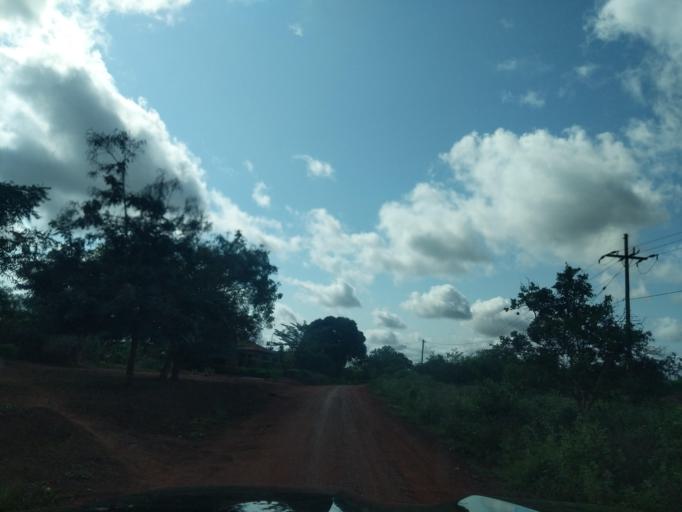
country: TZ
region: Tanga
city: Muheza
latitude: -5.4191
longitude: 38.6260
